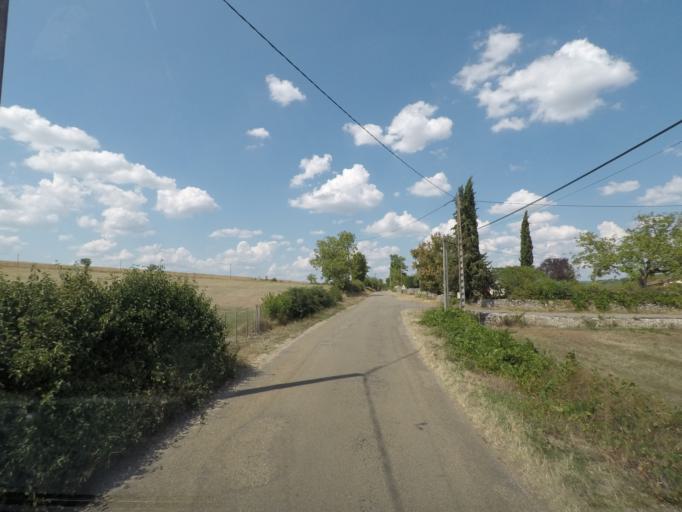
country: FR
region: Midi-Pyrenees
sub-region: Departement du Lot
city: Cahors
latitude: 44.5280
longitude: 1.6171
